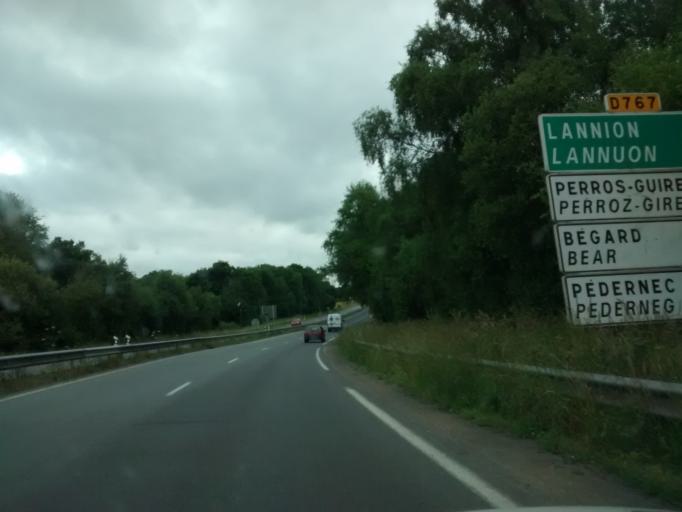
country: FR
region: Brittany
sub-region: Departement des Cotes-d'Armor
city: Graces
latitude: 48.5662
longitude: -3.2060
